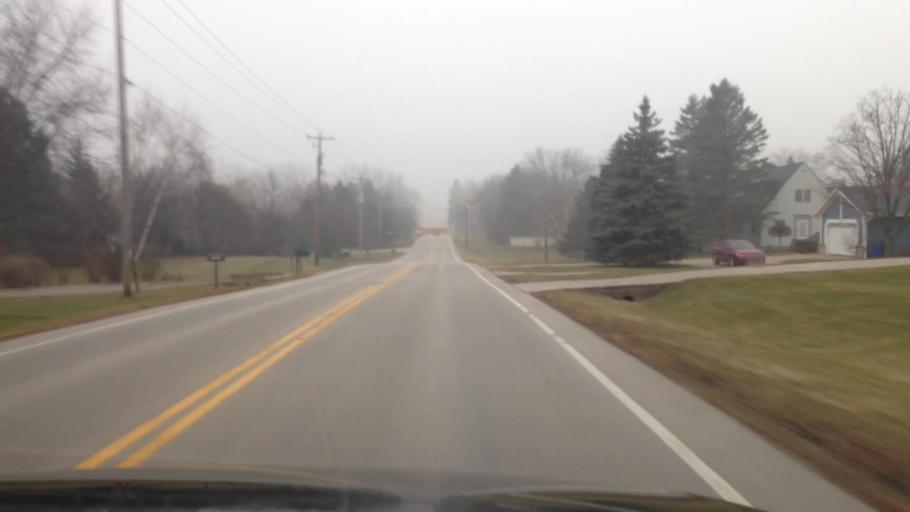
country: US
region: Wisconsin
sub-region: Milwaukee County
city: Hales Corners
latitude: 42.9182
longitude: -88.0775
